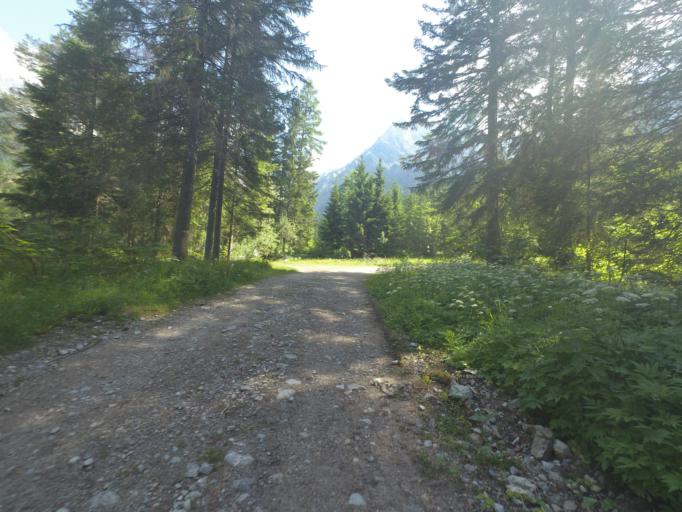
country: AT
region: Salzburg
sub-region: Politischer Bezirk Zell am See
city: Dienten am Hochkonig
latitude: 47.4186
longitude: 12.9908
